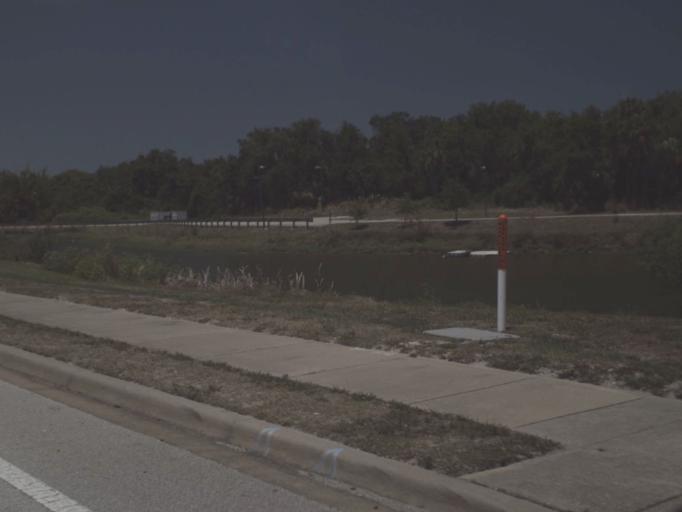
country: US
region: Florida
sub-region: Brevard County
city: Palm Bay
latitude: 28.0590
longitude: -80.5916
